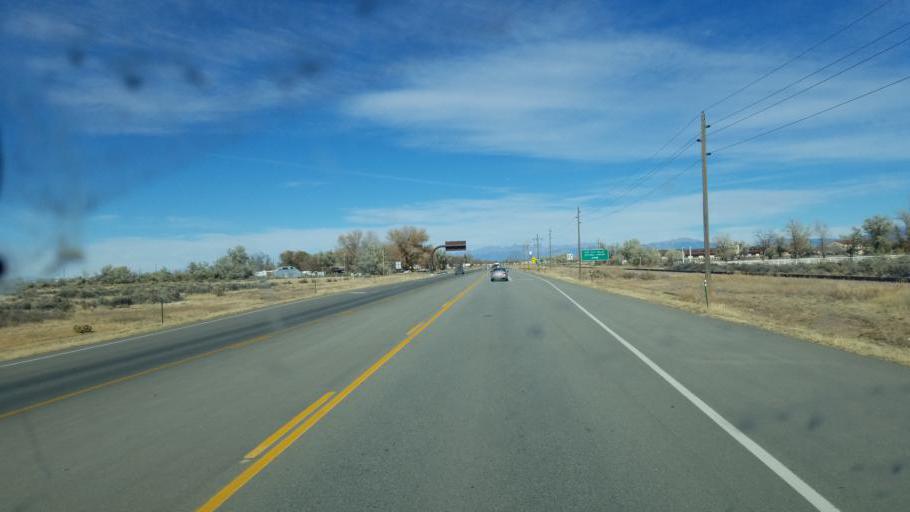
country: US
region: Colorado
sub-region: Alamosa County
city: Alamosa
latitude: 37.4420
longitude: -105.8845
